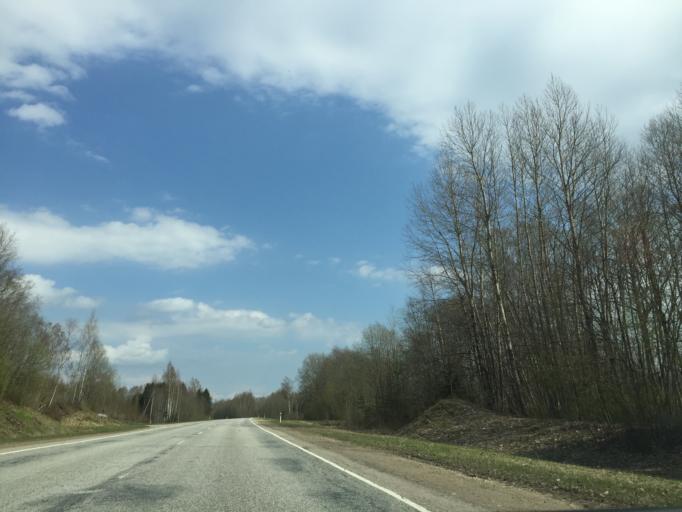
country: LV
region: Apes Novads
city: Ape
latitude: 57.5373
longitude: 26.8195
